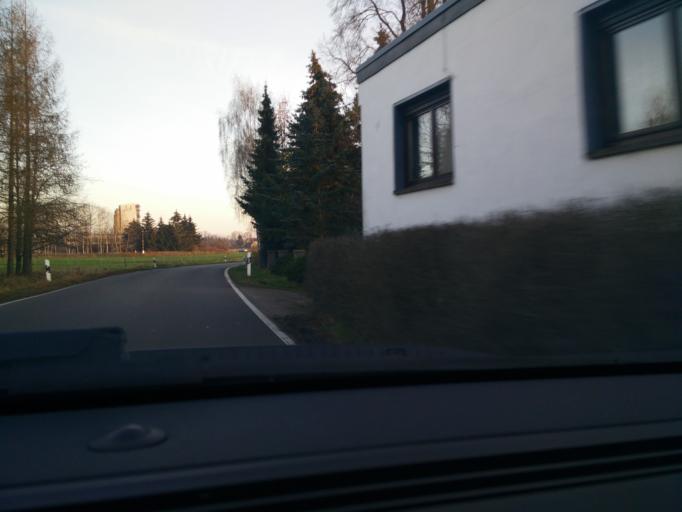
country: DE
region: Saxony
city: Bad Lausick
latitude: 51.1491
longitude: 12.6105
